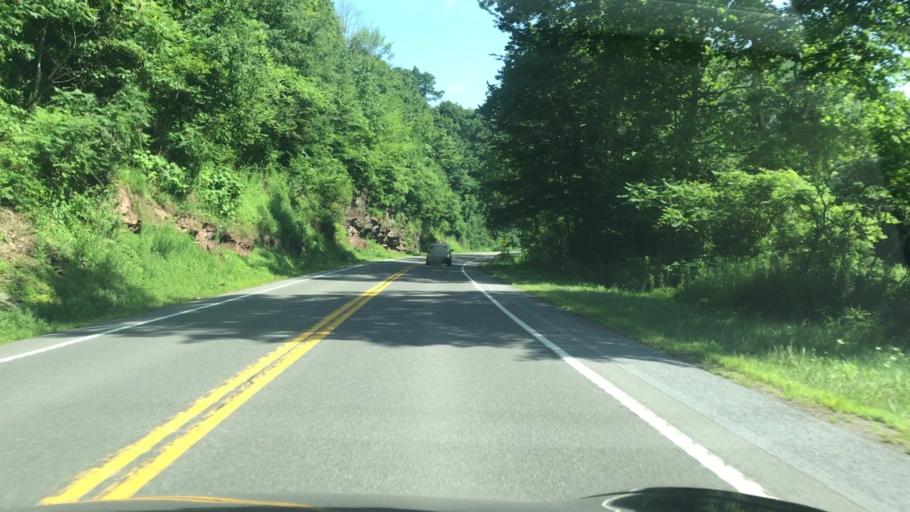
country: US
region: Pennsylvania
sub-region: Tioga County
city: Blossburg
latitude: 41.4819
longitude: -76.9796
